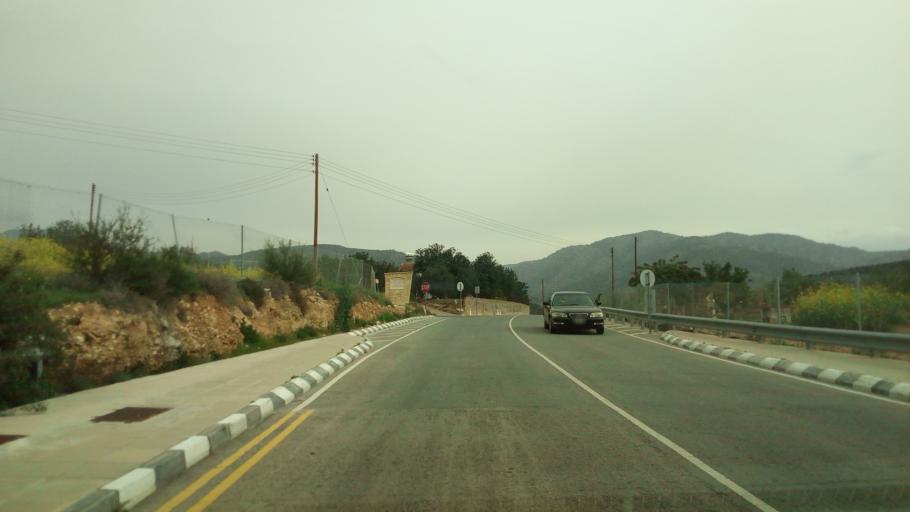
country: CY
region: Limassol
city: Mouttagiaka
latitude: 34.7474
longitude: 33.0841
